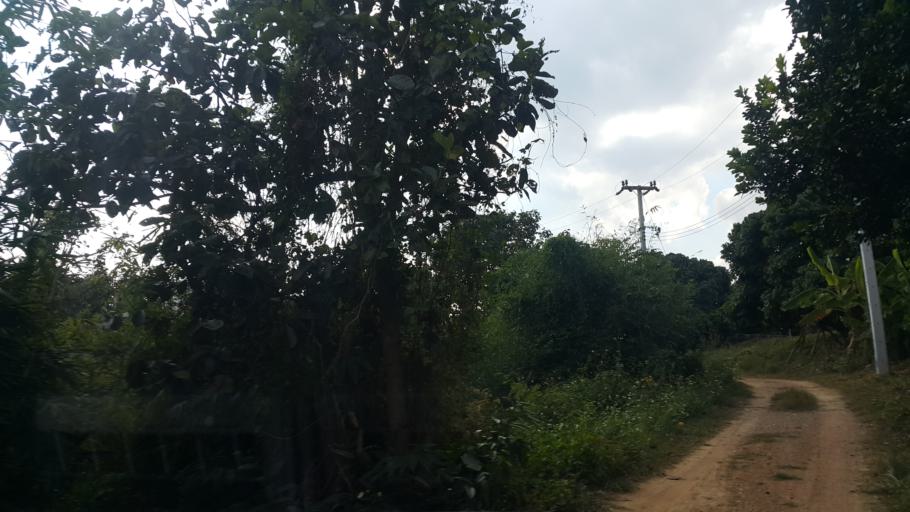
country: TH
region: Lamphun
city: Ban Thi
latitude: 18.5958
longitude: 99.1629
